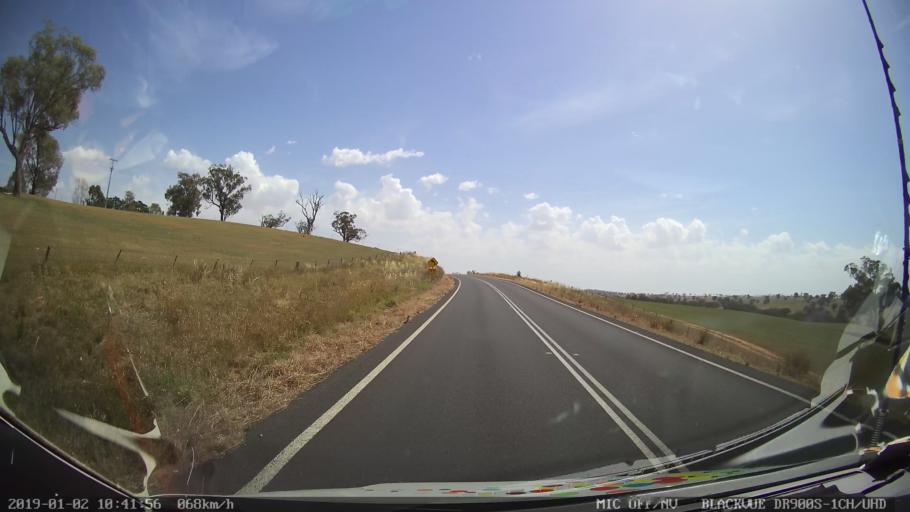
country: AU
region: New South Wales
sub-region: Cootamundra
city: Cootamundra
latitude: -34.7898
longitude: 148.3077
